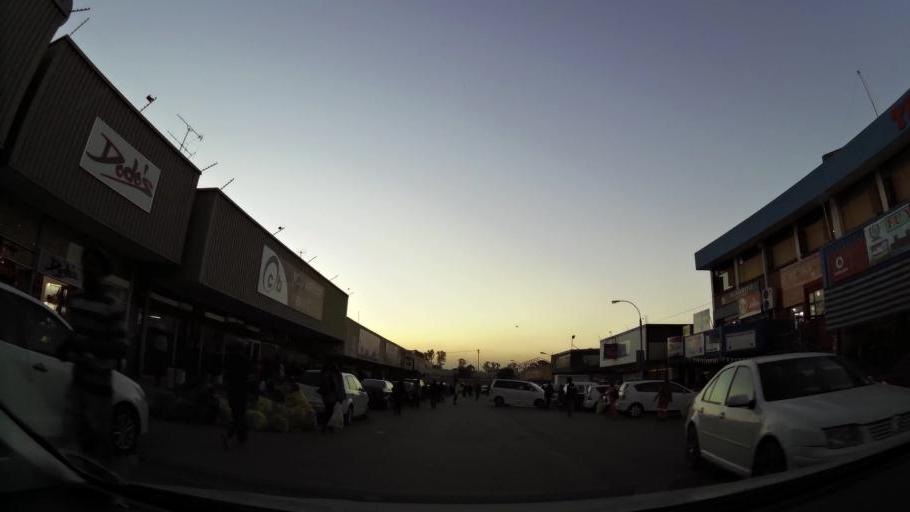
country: ZA
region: North-West
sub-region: Bojanala Platinum District Municipality
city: Rustenburg
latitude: -25.6637
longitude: 27.2379
